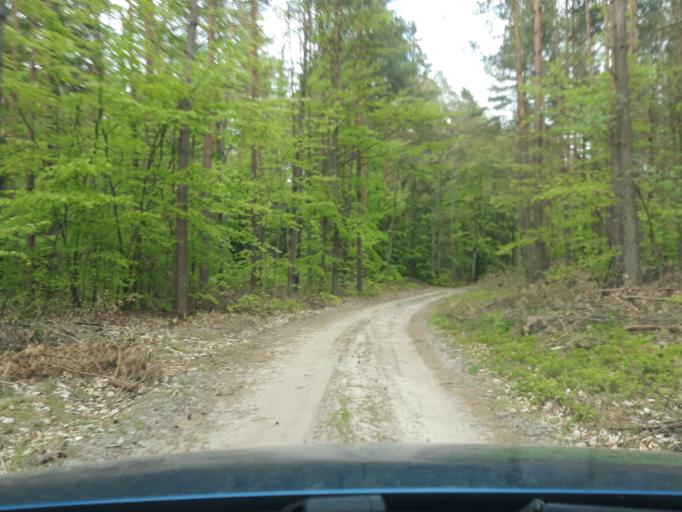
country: PL
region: Pomeranian Voivodeship
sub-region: Powiat czluchowski
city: Czluchow
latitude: 53.7567
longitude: 17.3460
